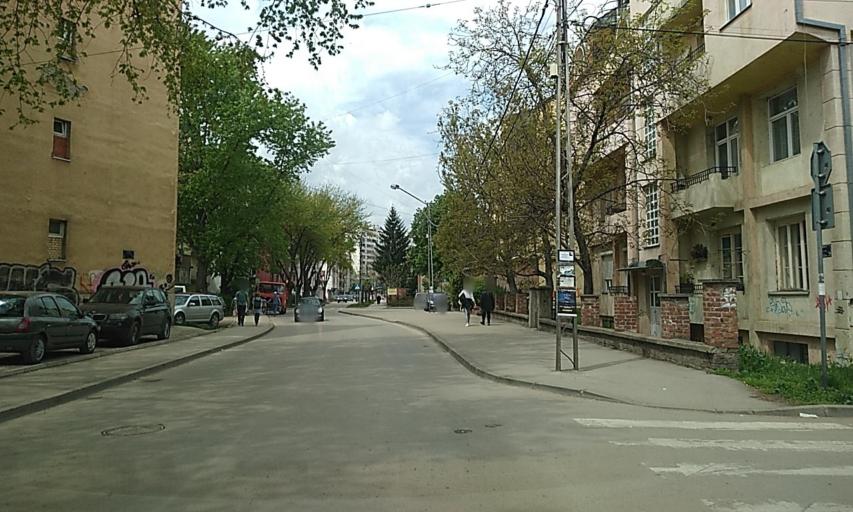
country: RS
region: Central Serbia
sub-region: Nisavski Okrug
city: Nis
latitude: 43.3193
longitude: 21.9140
